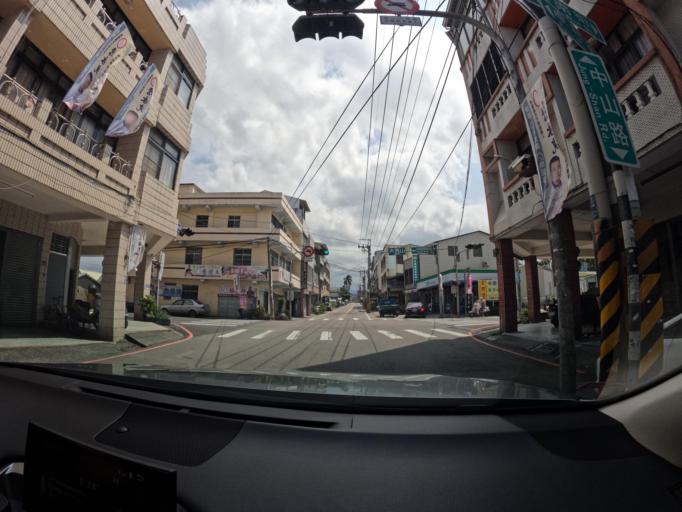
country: TW
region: Taiwan
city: Fengyuan
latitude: 24.3071
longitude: 120.8300
